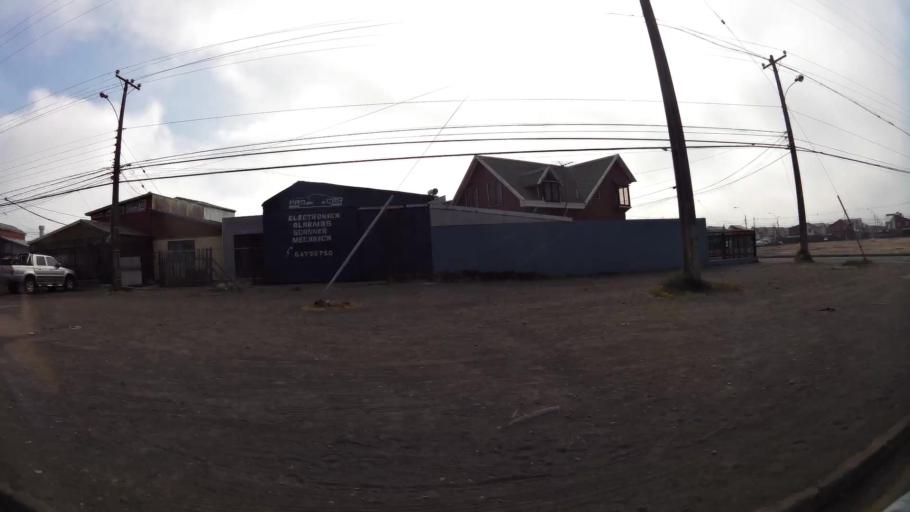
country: CL
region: Biobio
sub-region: Provincia de Concepcion
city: Concepcion
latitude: -36.7987
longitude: -73.1065
